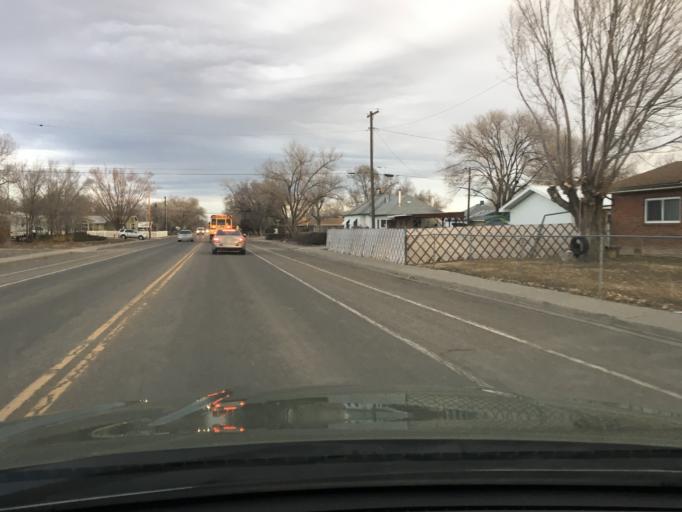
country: US
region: Colorado
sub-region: Montrose County
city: Montrose
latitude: 38.4733
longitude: -107.8661
